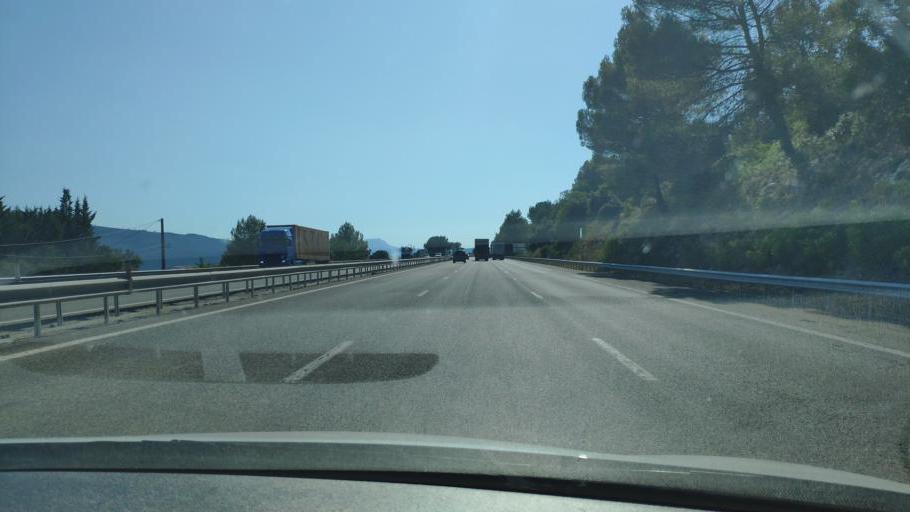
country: FR
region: Provence-Alpes-Cote d'Azur
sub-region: Departement du Var
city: Brignoles
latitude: 43.4205
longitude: 6.0599
